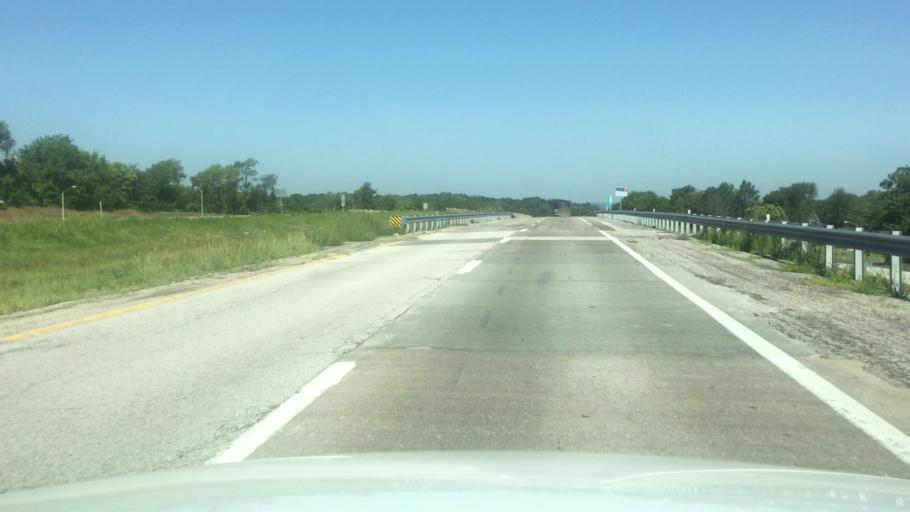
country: US
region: Missouri
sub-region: Buchanan County
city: Saint Joseph
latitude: 39.7210
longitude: -94.8324
